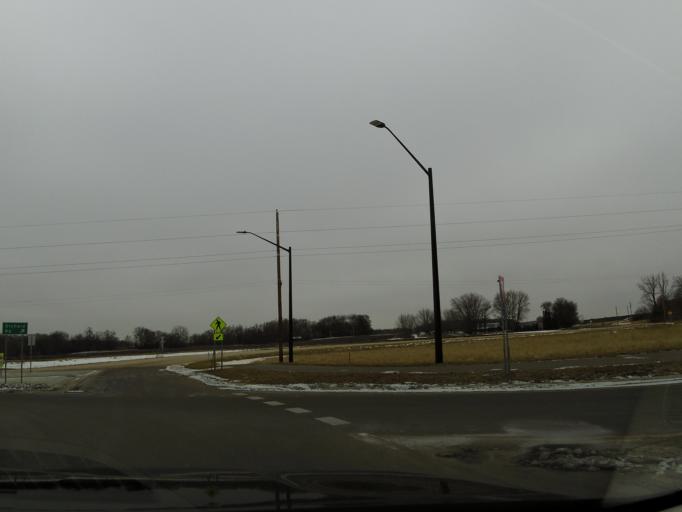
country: US
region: Minnesota
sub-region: Carver County
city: Waconia
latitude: 44.8292
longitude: -93.8238
